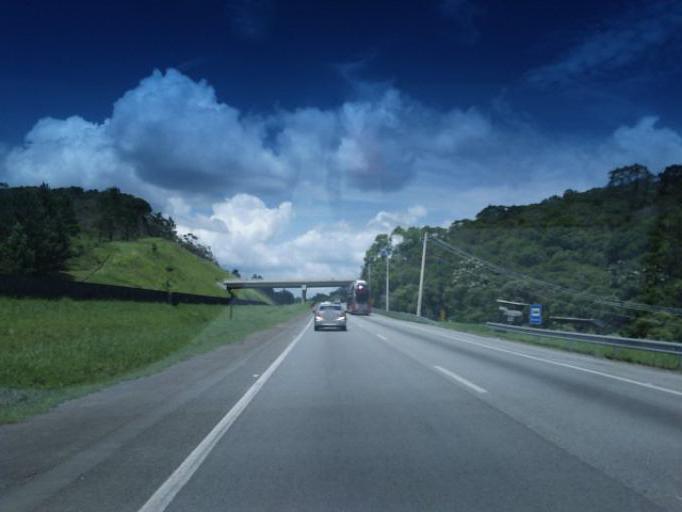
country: BR
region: Sao Paulo
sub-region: Juquitiba
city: Juquitiba
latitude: -23.9554
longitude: -47.1092
